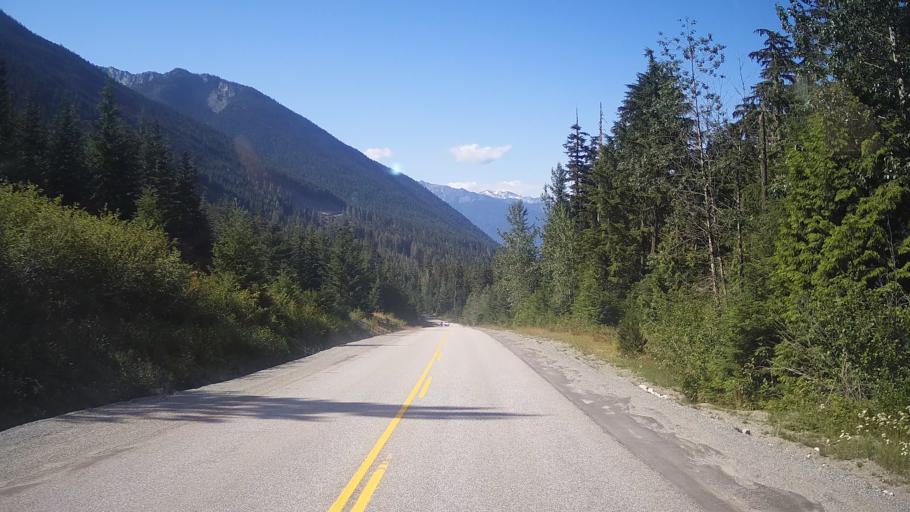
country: CA
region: British Columbia
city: Pemberton
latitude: 50.3518
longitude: -122.5319
